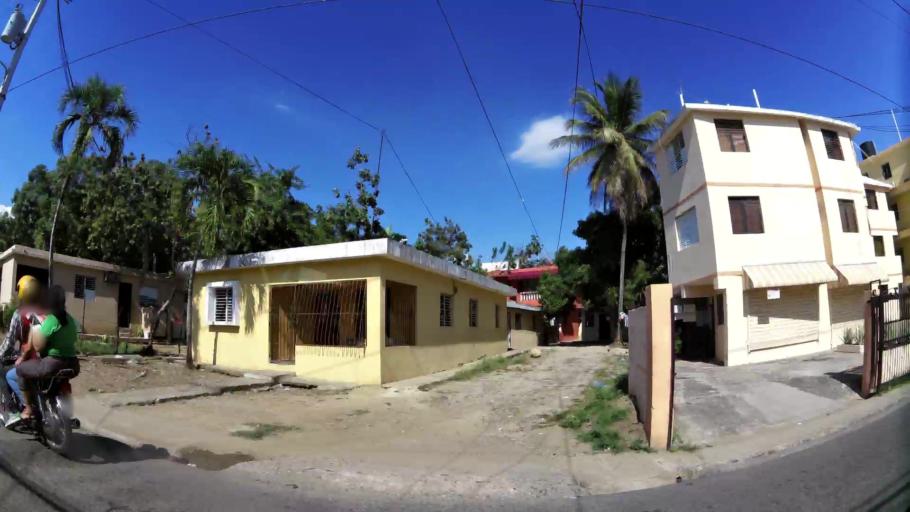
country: DO
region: Santo Domingo
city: Santo Domingo Oeste
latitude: 18.4664
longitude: -69.9985
